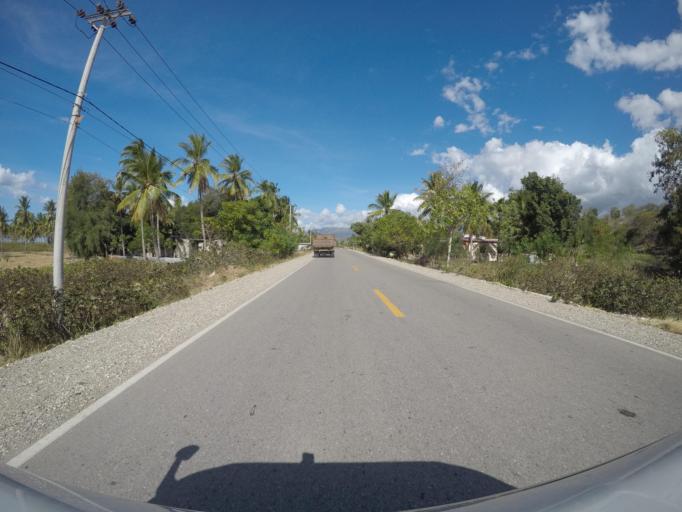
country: TL
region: Baucau
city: Baucau
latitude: -8.4766
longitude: 126.5405
